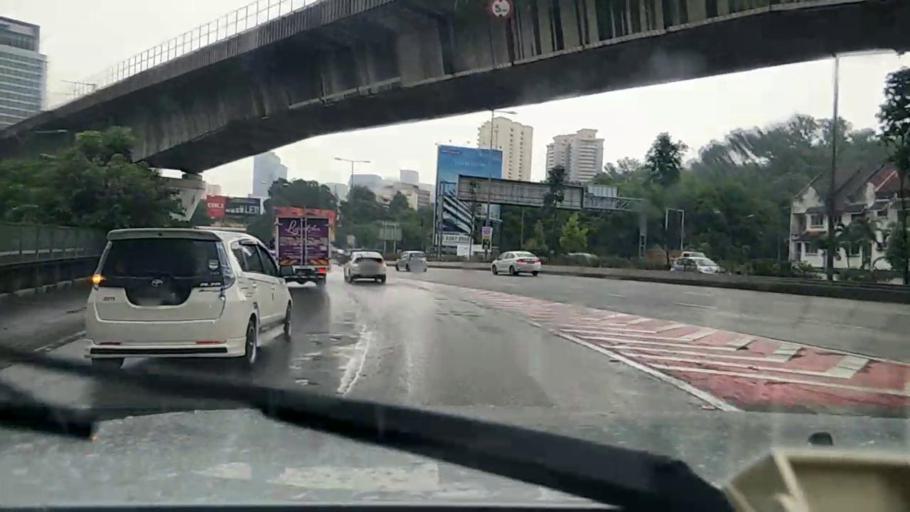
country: MY
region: Kuala Lumpur
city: Kuala Lumpur
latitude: 3.1172
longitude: 101.6792
